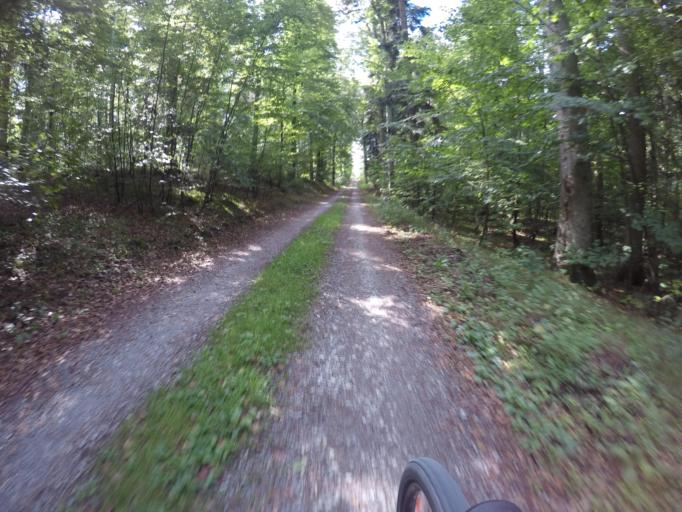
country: DE
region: Baden-Wuerttemberg
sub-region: Karlsruhe Region
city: Gechingen
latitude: 48.6793
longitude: 8.8217
